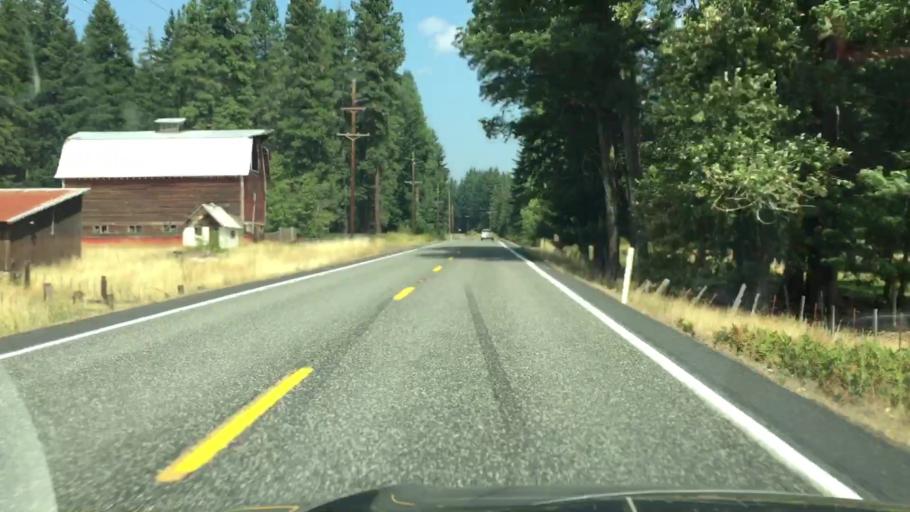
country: US
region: Washington
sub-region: Klickitat County
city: White Salmon
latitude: 45.9557
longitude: -121.4897
